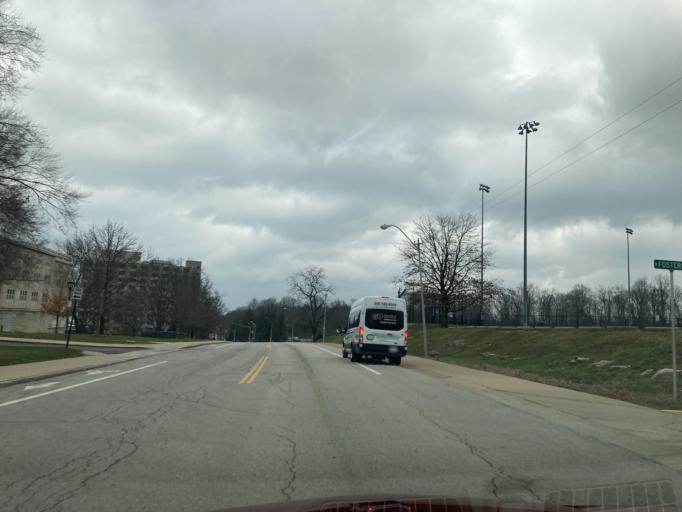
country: US
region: Indiana
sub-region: Monroe County
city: Bloomington
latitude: 39.1764
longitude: -86.5189
